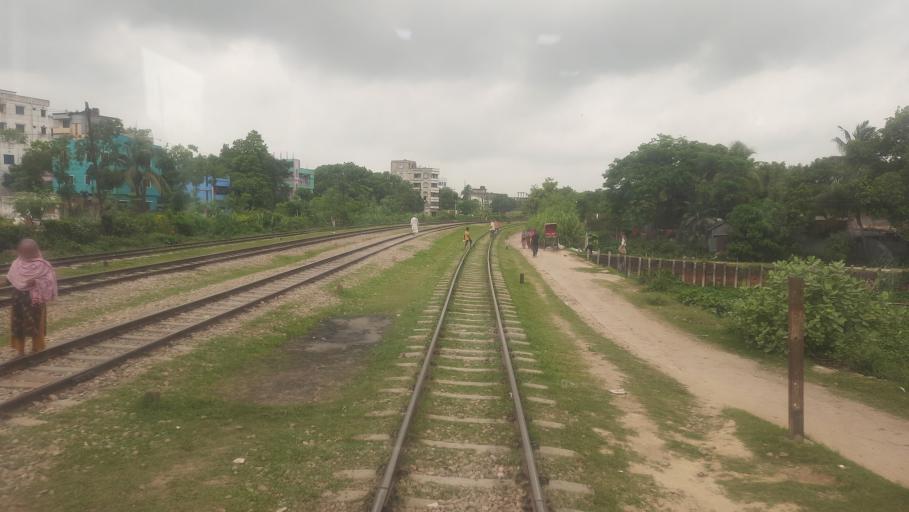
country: BD
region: Dhaka
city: Bhairab Bazar
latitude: 23.9659
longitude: 91.1061
